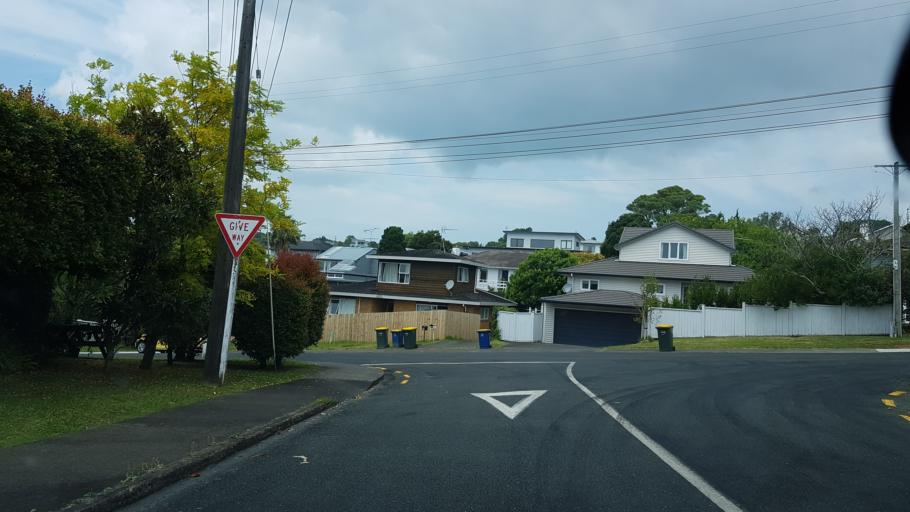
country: NZ
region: Auckland
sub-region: Auckland
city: North Shore
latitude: -36.7985
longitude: 174.7728
